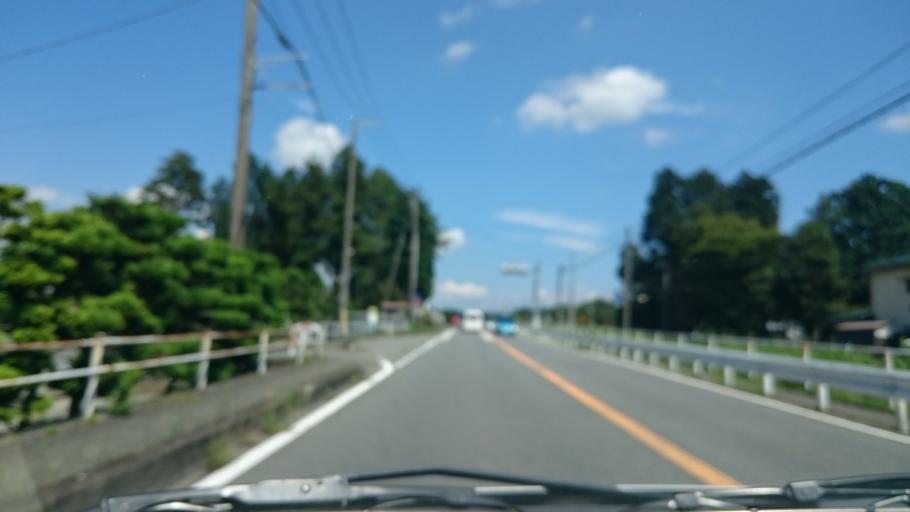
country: JP
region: Shizuoka
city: Gotemba
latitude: 35.2784
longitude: 138.9261
